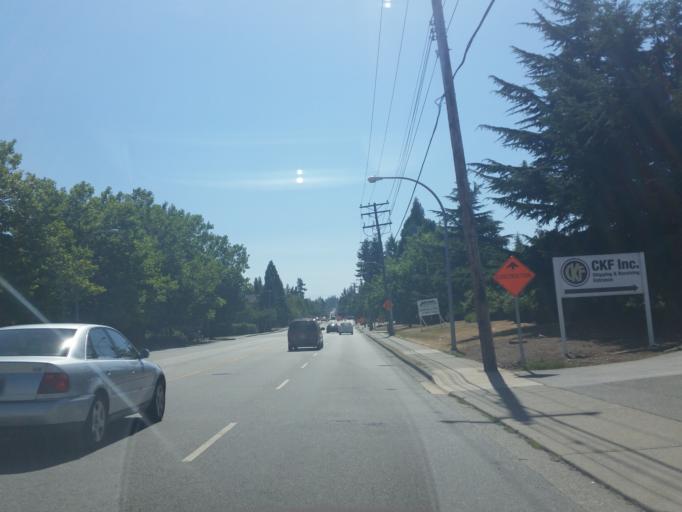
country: CA
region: British Columbia
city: Langley
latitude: 49.1077
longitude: -122.6689
